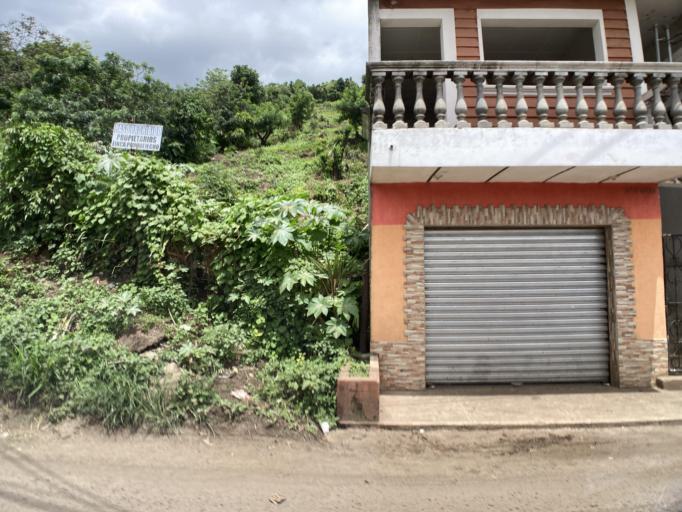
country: GT
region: Guatemala
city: Villa Canales
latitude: 14.4512
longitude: -90.5671
